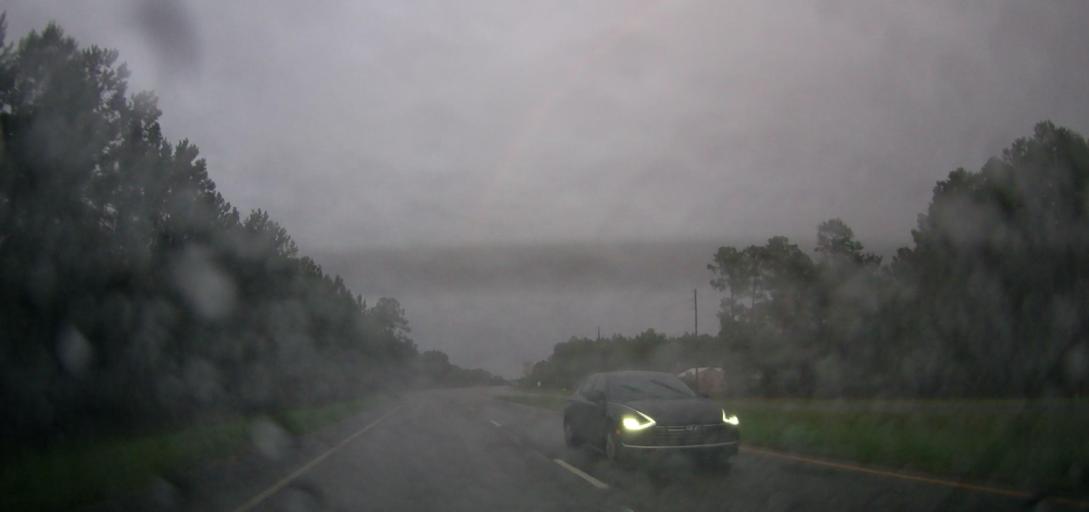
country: US
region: Georgia
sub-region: Clinch County
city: Homerville
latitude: 30.9844
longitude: -82.8855
